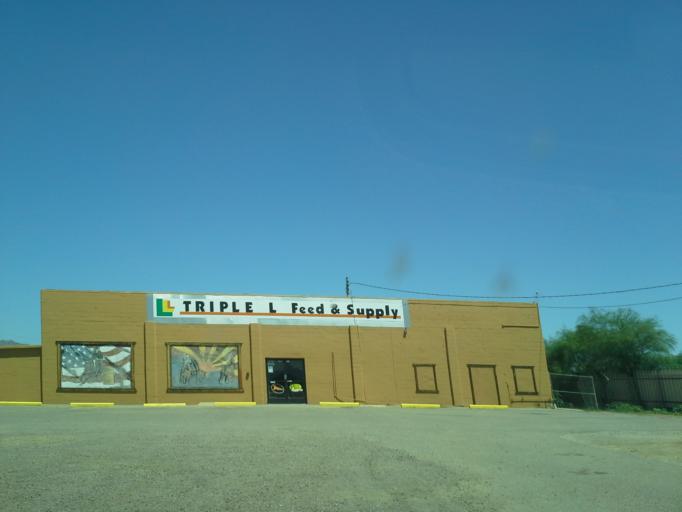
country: US
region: Arizona
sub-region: Pima County
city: Marana
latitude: 32.4552
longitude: -111.2168
